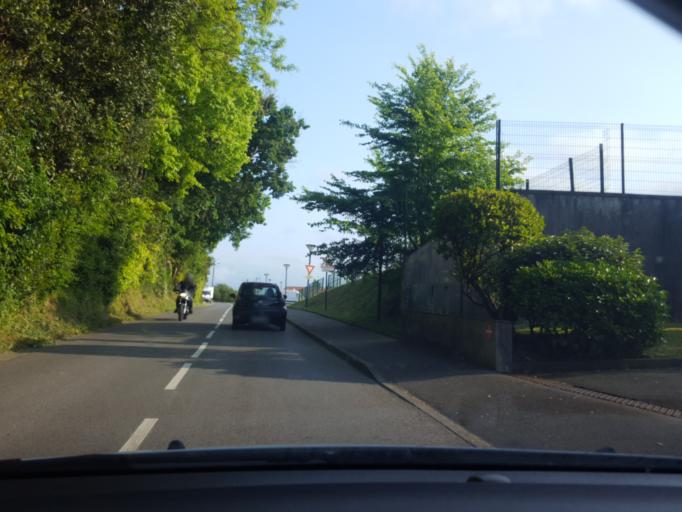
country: FR
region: Aquitaine
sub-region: Departement des Landes
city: Ondres
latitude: 43.5626
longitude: -1.4449
